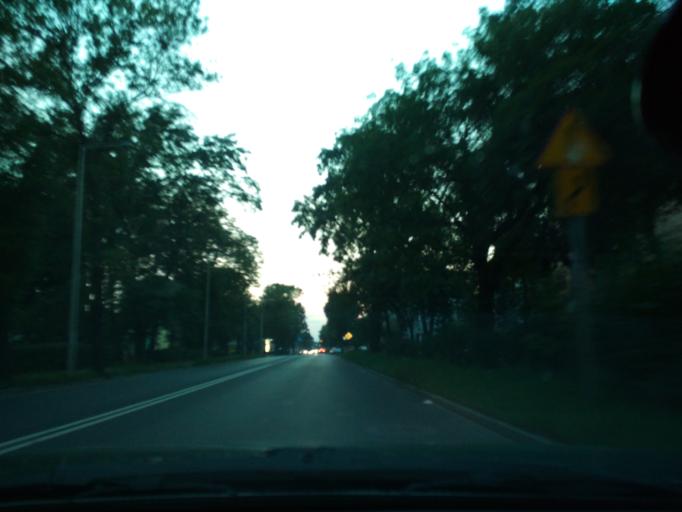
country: PL
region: Silesian Voivodeship
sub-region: Powiat zawiercianski
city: Zawiercie
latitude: 50.4813
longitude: 19.4383
